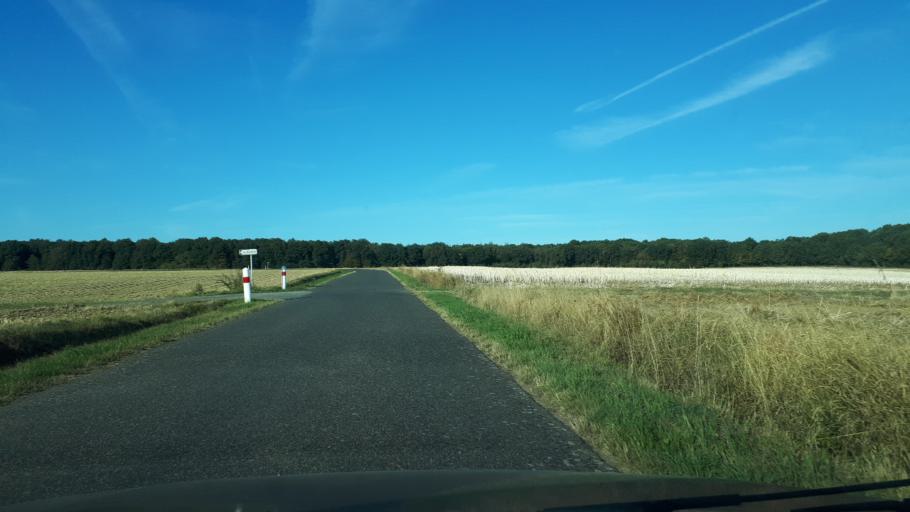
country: FR
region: Centre
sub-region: Departement du Loir-et-Cher
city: Montoire-sur-le-Loir
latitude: 47.7117
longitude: 0.9290
